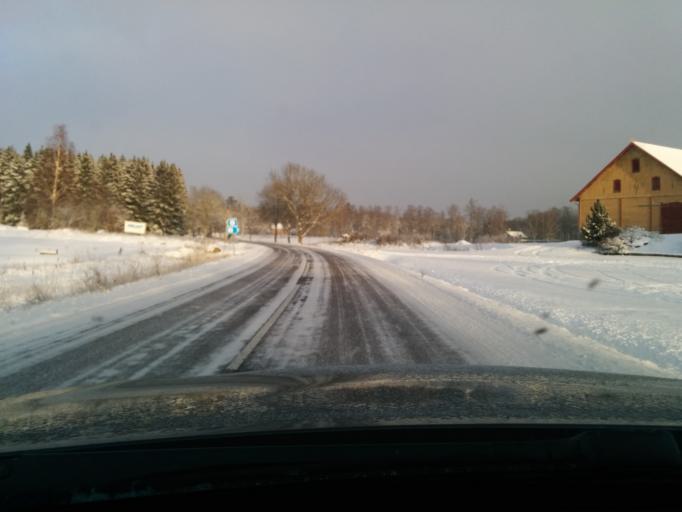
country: SE
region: Uppsala
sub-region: Tierps Kommun
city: Orbyhus
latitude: 60.1998
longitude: 17.6996
